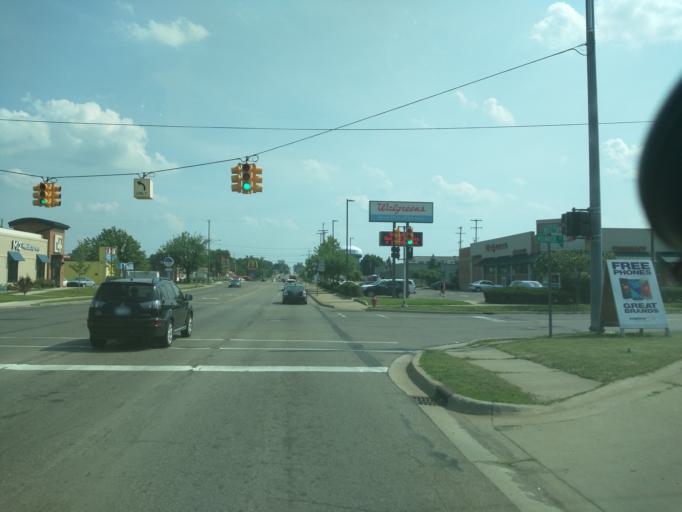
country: US
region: Michigan
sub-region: Jackson County
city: Jackson
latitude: 42.2654
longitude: -84.4234
